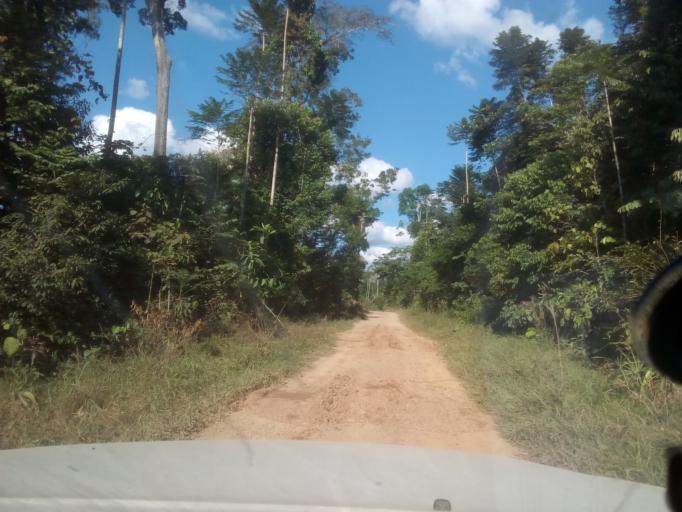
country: PE
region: Cusco
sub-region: Provincia de Quispicanchis
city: Quince Mil
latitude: -12.6511
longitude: -70.3508
